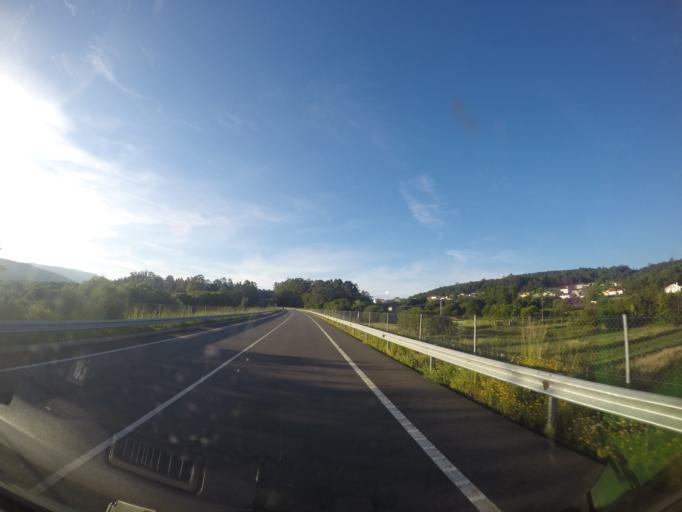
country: ES
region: Galicia
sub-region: Provincia da Coruna
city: Noia
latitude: 42.8036
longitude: -8.8888
